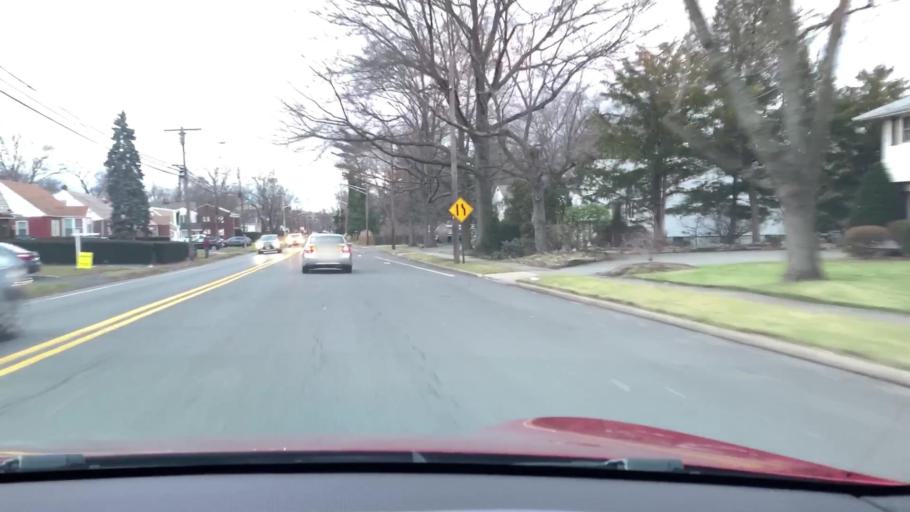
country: US
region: New Jersey
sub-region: Bergen County
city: Demarest
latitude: 40.9481
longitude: -73.9761
